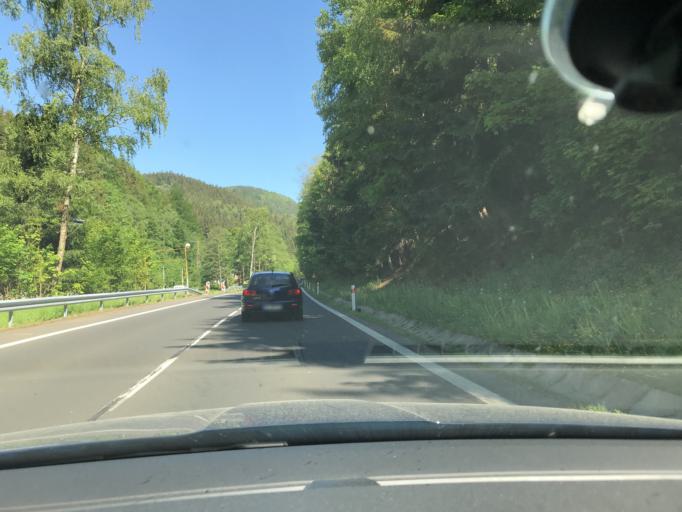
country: CZ
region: Karlovarsky
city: Jachymov
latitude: 50.3422
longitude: 12.9362
